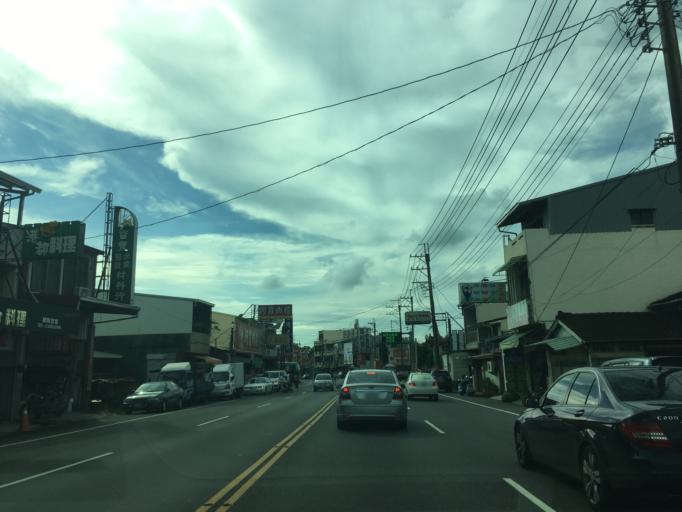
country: TW
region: Taiwan
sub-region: Chiayi
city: Jiayi Shi
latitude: 23.4488
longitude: 120.4903
